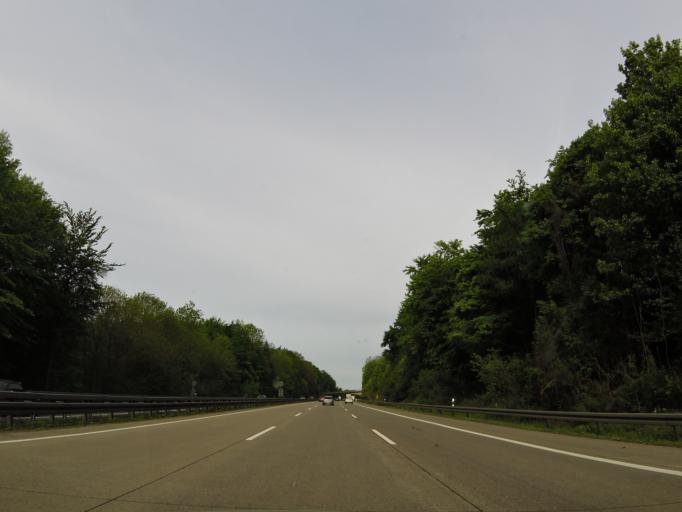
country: DE
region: Lower Saxony
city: Schellerten
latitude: 52.1208
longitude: 10.0805
